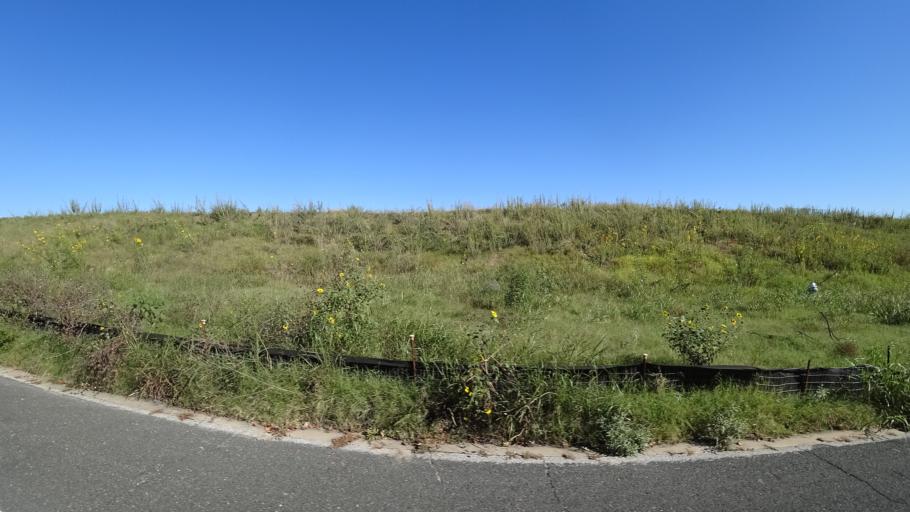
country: US
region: Texas
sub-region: Travis County
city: Austin
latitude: 30.2897
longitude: -97.6931
